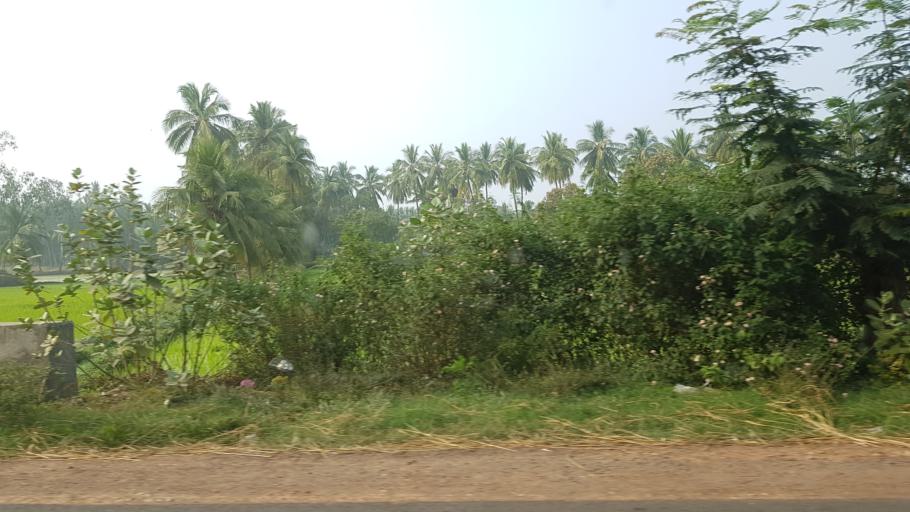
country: IN
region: Andhra Pradesh
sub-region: West Godavari
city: Akividu
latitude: 16.5334
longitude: 81.3949
